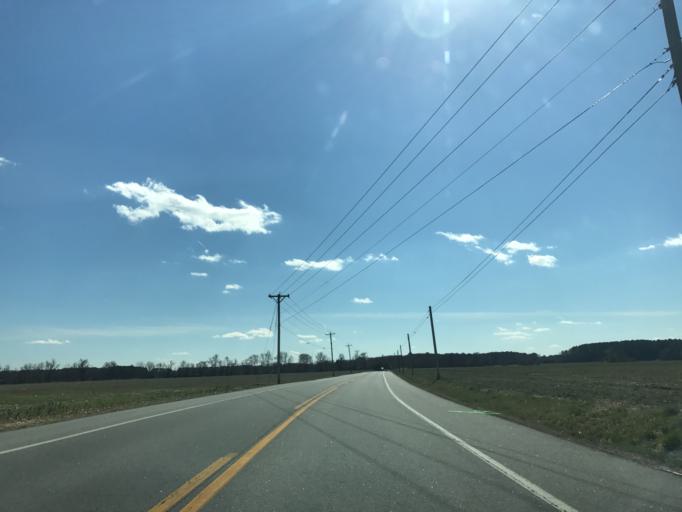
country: US
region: Maryland
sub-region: Kent County
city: Rock Hall
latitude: 39.1657
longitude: -76.2013
